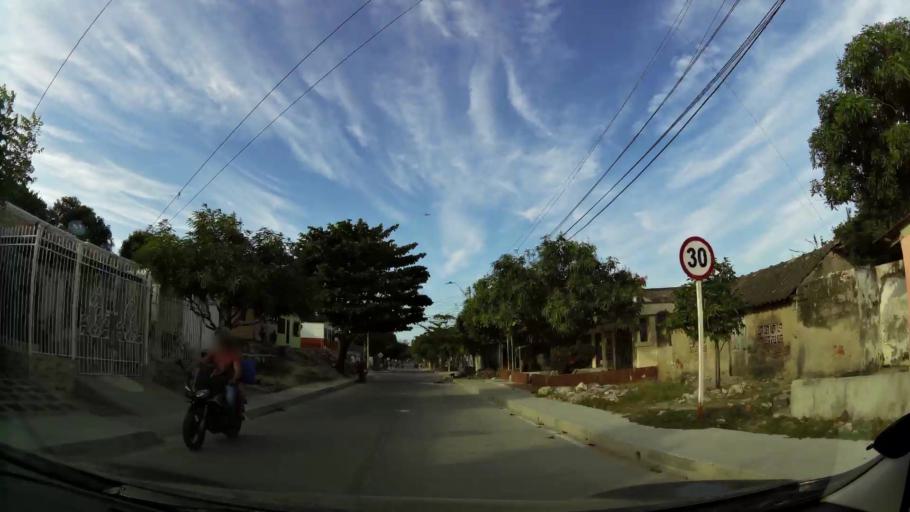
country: CO
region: Atlantico
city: Barranquilla
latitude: 10.9375
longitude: -74.8225
